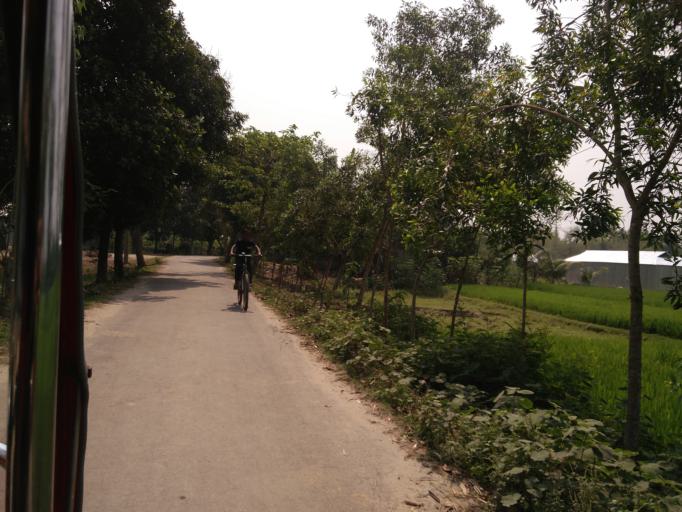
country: BD
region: Dhaka
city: Muktagacha
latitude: 24.8867
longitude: 90.2757
